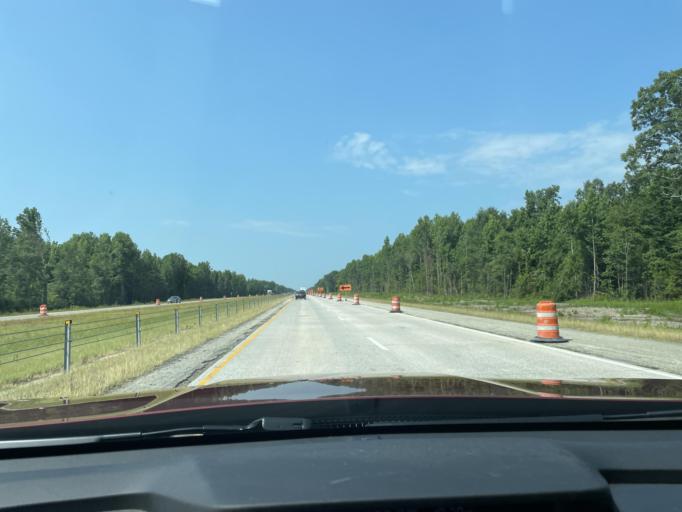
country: US
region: Arkansas
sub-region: White County
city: Searcy
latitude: 35.1839
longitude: -91.7551
